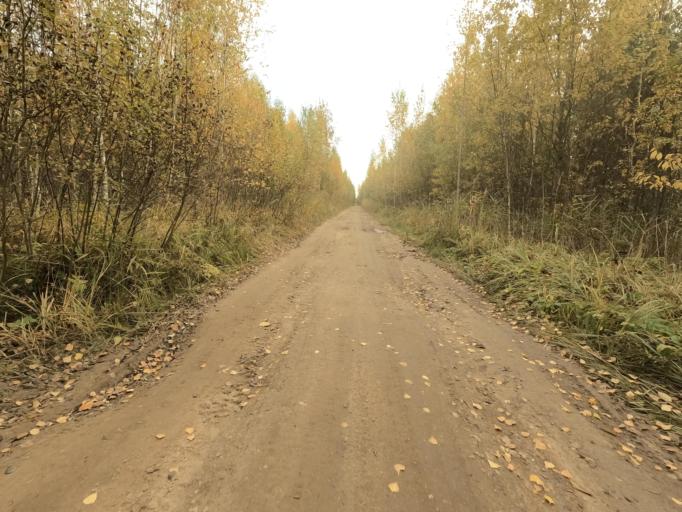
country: RU
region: Novgorod
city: Pankovka
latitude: 58.8772
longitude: 30.8651
